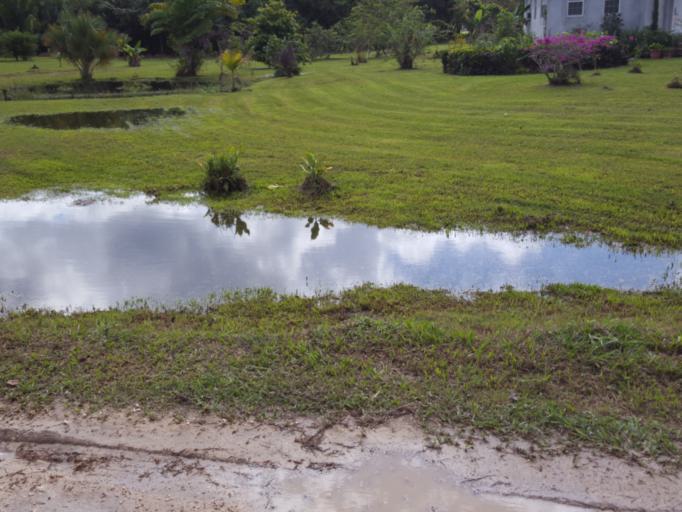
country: BZ
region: Belize
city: Belize City
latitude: 17.5708
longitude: -88.4061
